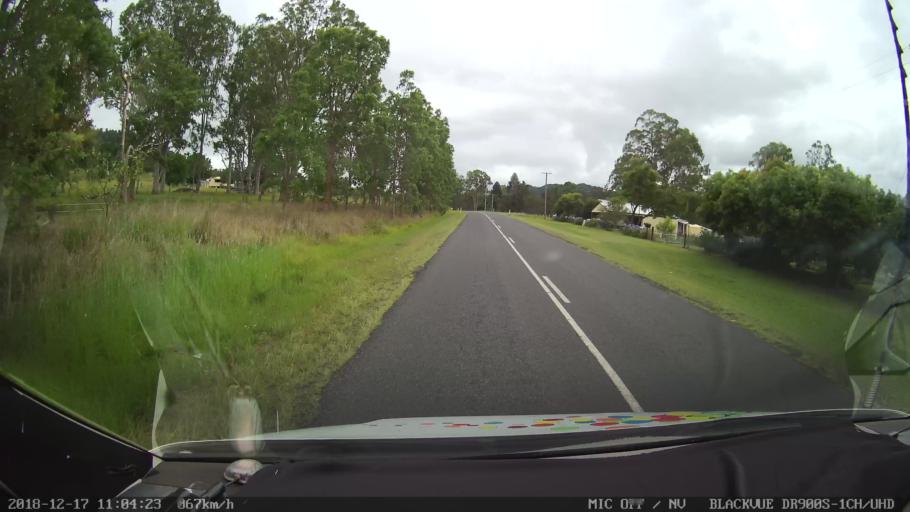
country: AU
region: New South Wales
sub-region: Kyogle
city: Kyogle
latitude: -28.7993
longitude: 152.6425
